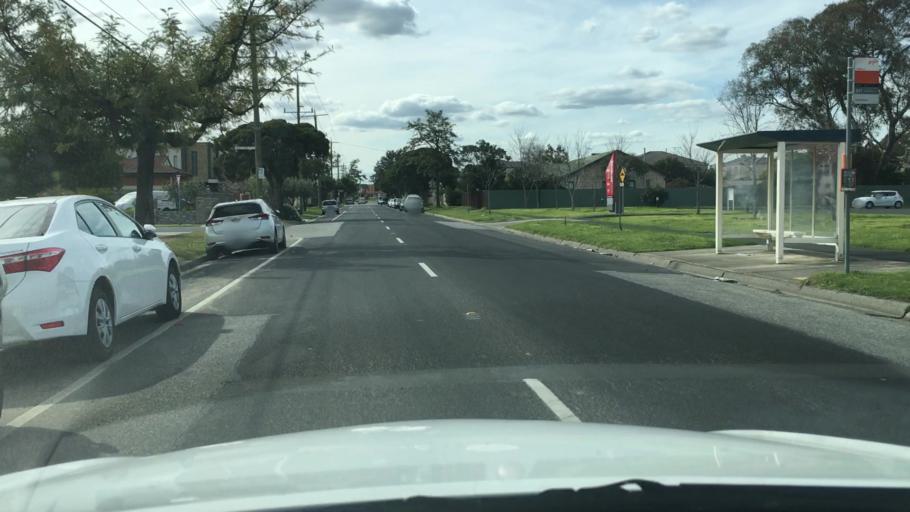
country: AU
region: Victoria
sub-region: Greater Dandenong
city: Springvale
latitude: -37.9566
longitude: 145.1576
